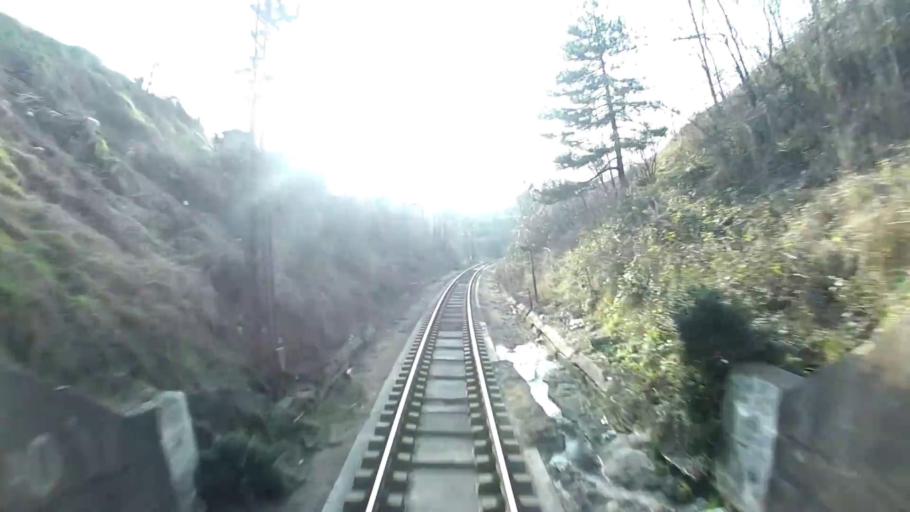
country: BG
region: Plovdiv
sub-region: Obshtina Karlovo
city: Klisura
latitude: 42.6954
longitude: 24.4754
